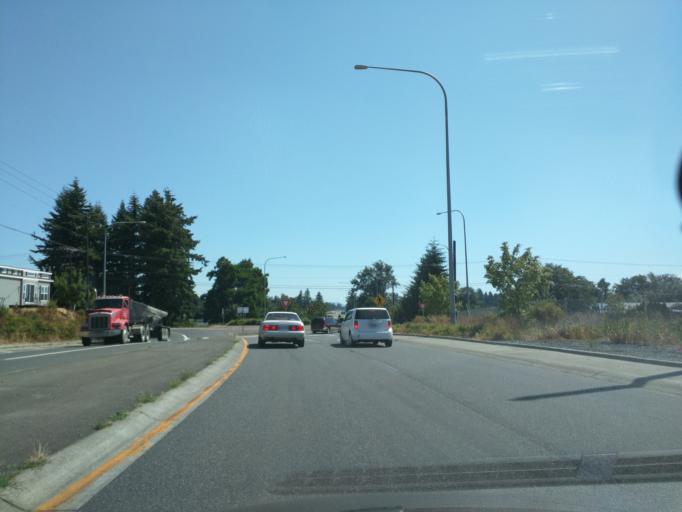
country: US
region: Washington
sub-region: Whatcom County
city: Lynden
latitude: 48.9078
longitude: -122.4857
